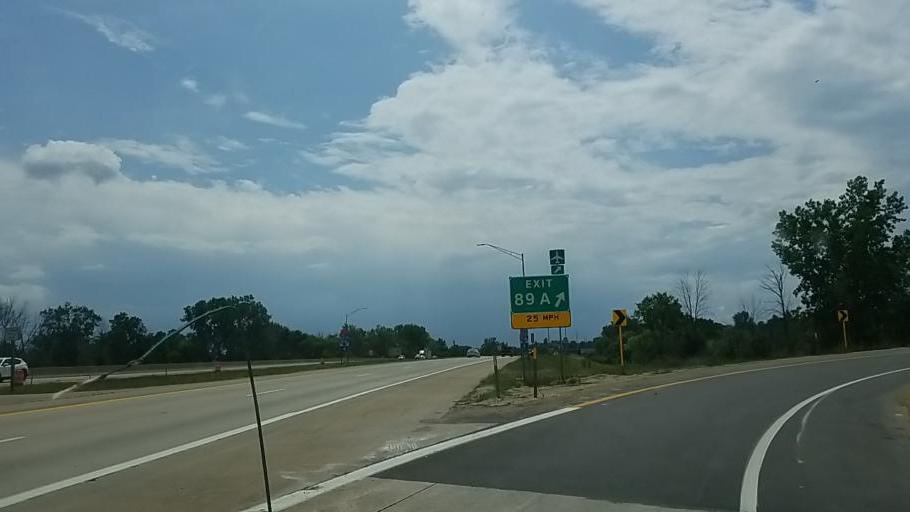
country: US
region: Michigan
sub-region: Kent County
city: Comstock Park
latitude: 43.0190
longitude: -85.6703
